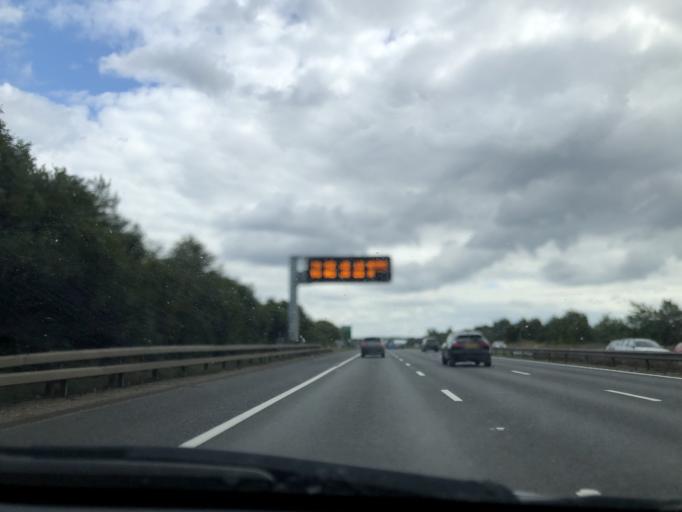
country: GB
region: England
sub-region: Kent
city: Dartford
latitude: 51.4279
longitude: 0.2155
